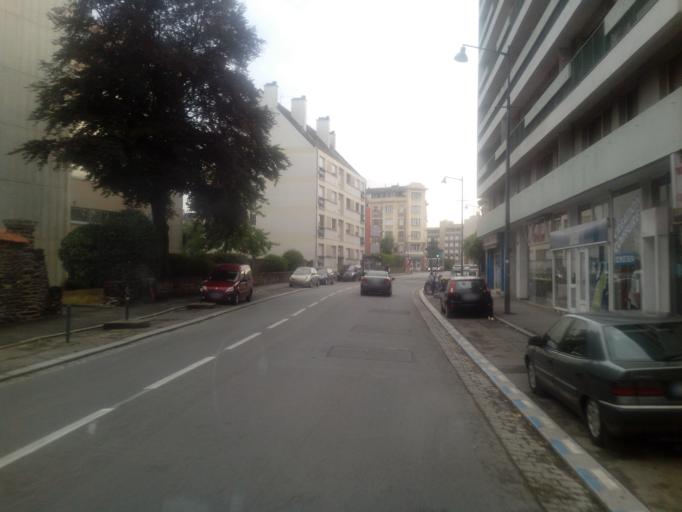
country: FR
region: Brittany
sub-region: Departement d'Ille-et-Vilaine
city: Rennes
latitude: 48.1201
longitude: -1.6658
